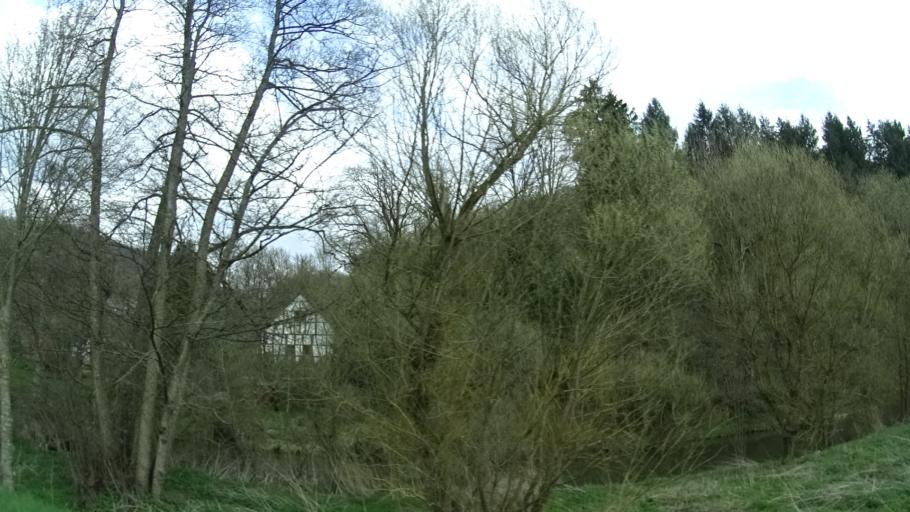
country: DE
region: Rheinland-Pfalz
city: Kellenbach
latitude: 49.8422
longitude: 7.4955
